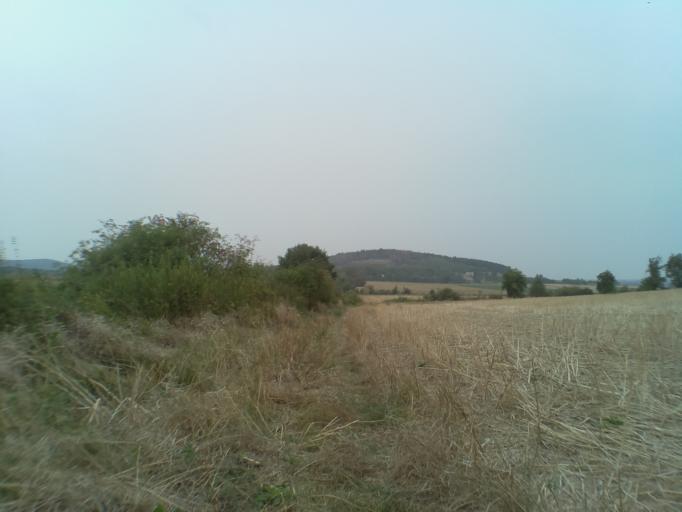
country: PL
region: Lower Silesian Voivodeship
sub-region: Powiat swidnicki
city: Strzegom
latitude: 50.9930
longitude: 16.2920
